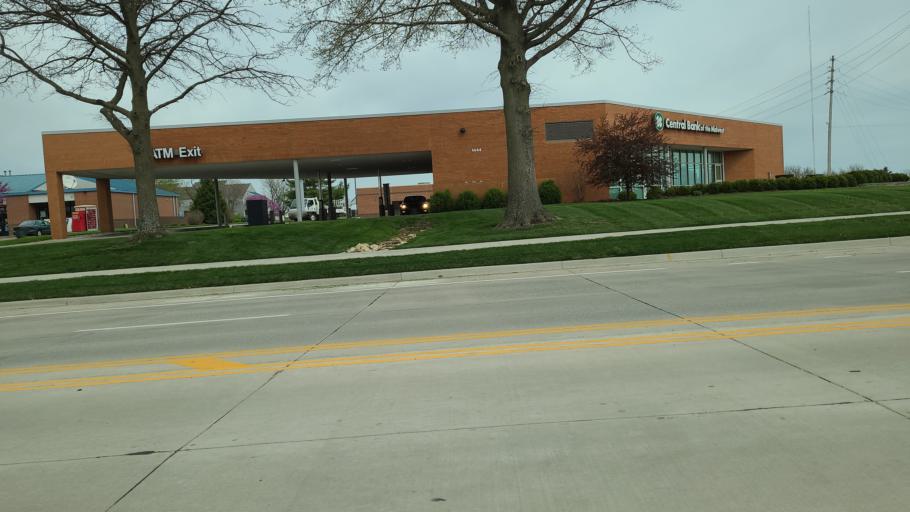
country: US
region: Kansas
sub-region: Douglas County
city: Lawrence
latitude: 38.9574
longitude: -95.2791
